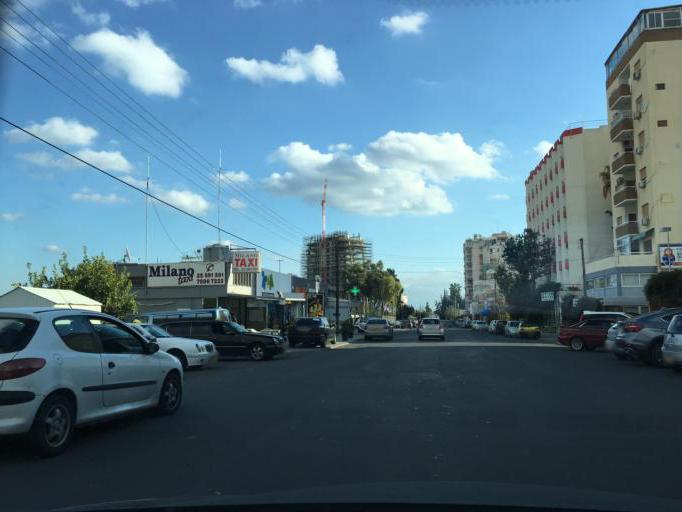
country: CY
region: Limassol
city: Limassol
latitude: 34.6926
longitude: 33.0675
